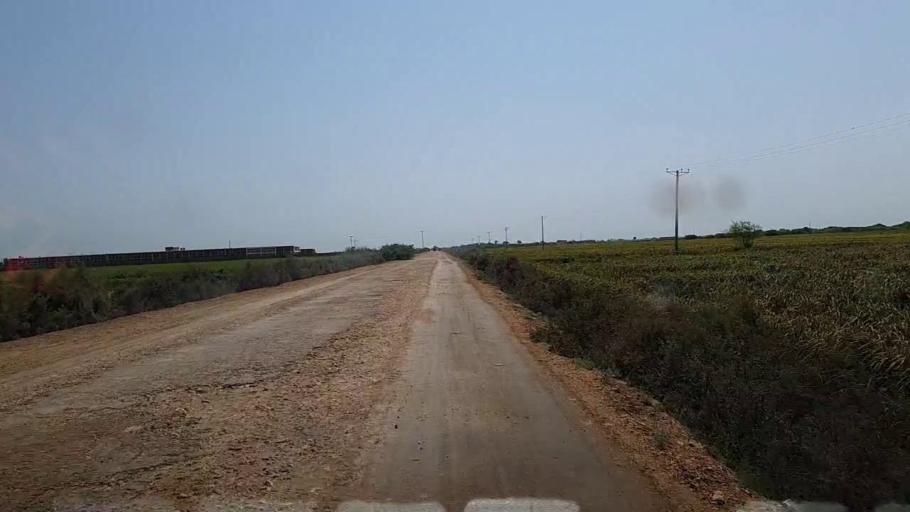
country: PK
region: Sindh
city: Mirpur Batoro
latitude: 24.6380
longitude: 68.4522
